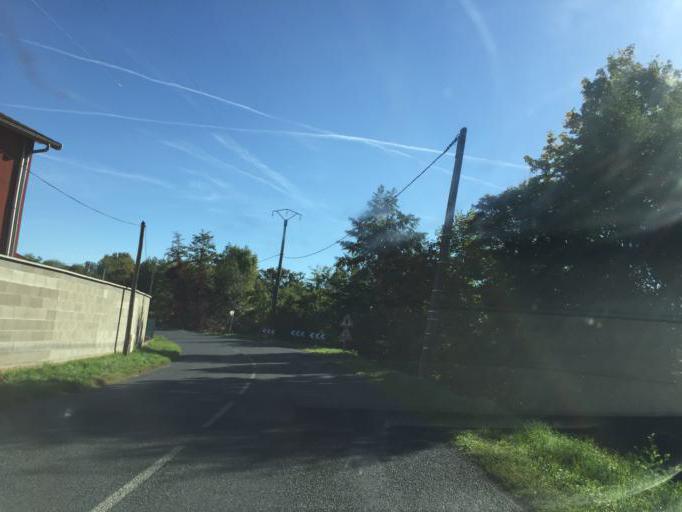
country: FR
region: Rhone-Alpes
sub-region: Departement du Rhone
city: Blace
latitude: 46.0563
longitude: 4.6351
